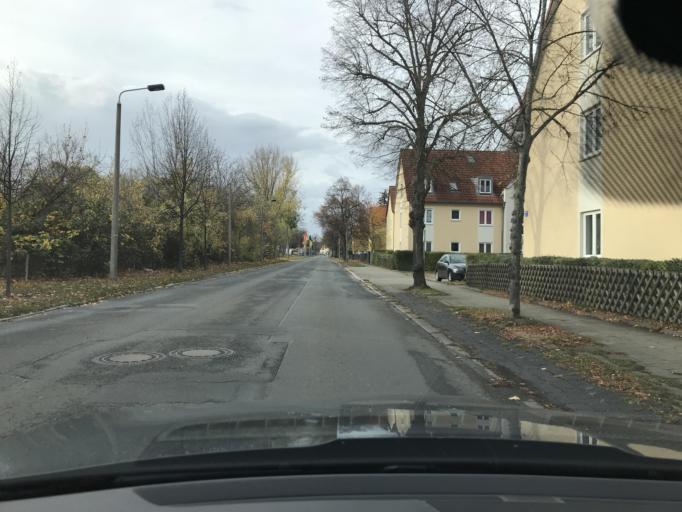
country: DE
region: Saxony-Anhalt
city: Halberstadt
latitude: 51.8826
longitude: 11.0621
